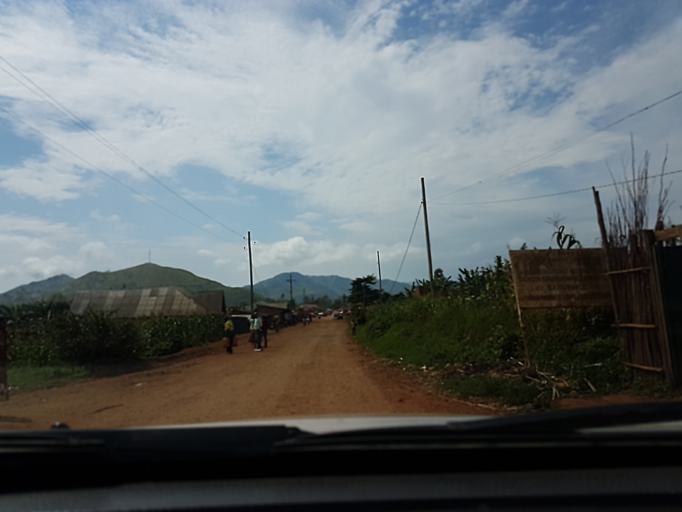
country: CD
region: South Kivu
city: Bukavu
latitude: -2.6567
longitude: 28.8738
